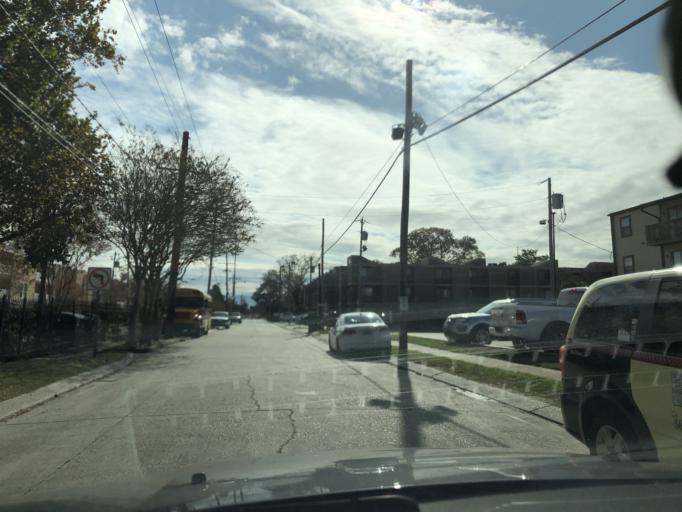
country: US
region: Louisiana
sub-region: Jefferson Parish
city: Metairie
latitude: 29.9945
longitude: -90.1610
